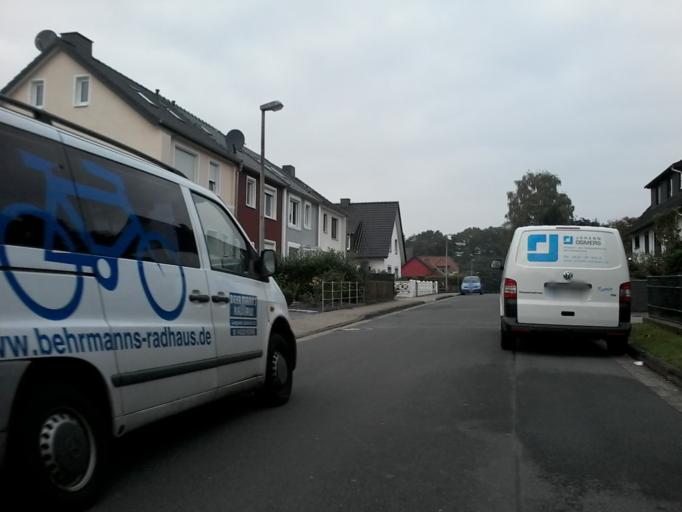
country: DE
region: Lower Saxony
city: Ahsen-Oetzen
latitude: 52.9995
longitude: 9.0721
